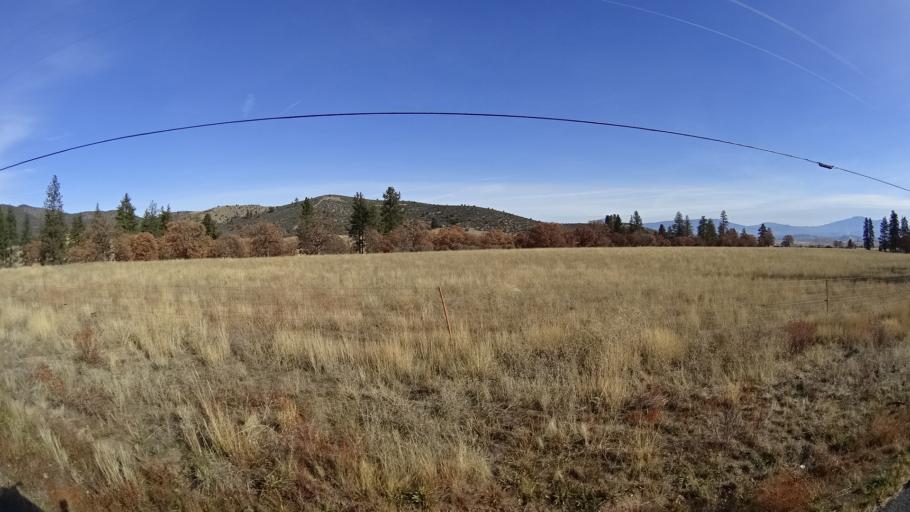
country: US
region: California
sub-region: Siskiyou County
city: Montague
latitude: 41.5401
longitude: -122.5883
